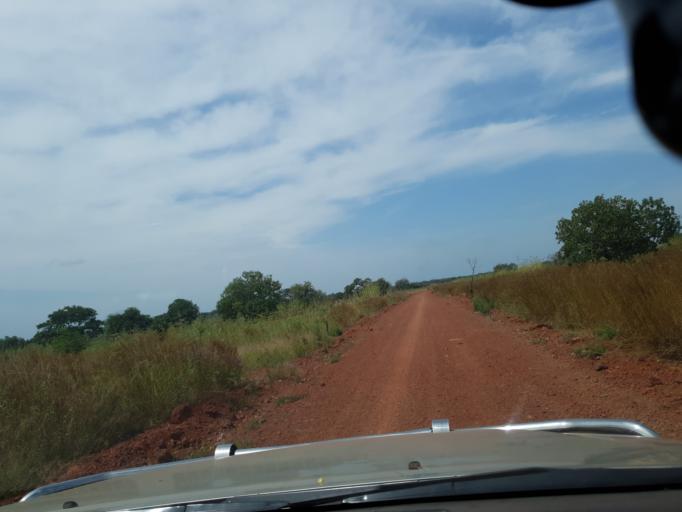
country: ML
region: Sikasso
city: Sikasso
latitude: 11.6397
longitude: -6.0959
